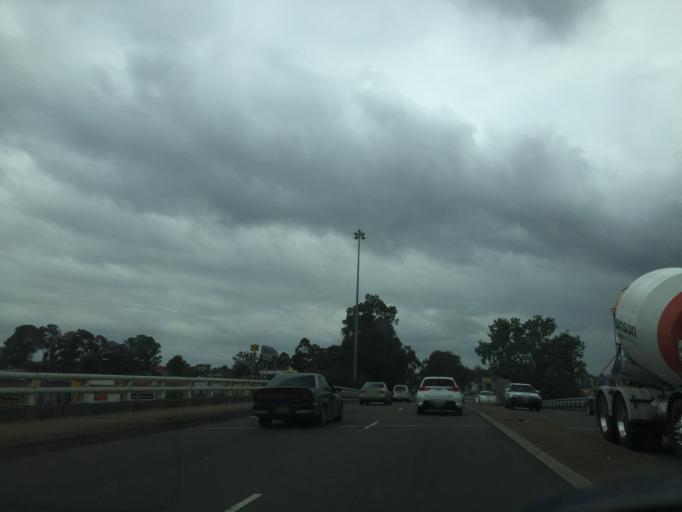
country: AU
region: New South Wales
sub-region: Blacktown
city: Blacktown
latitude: -33.7739
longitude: 150.9355
